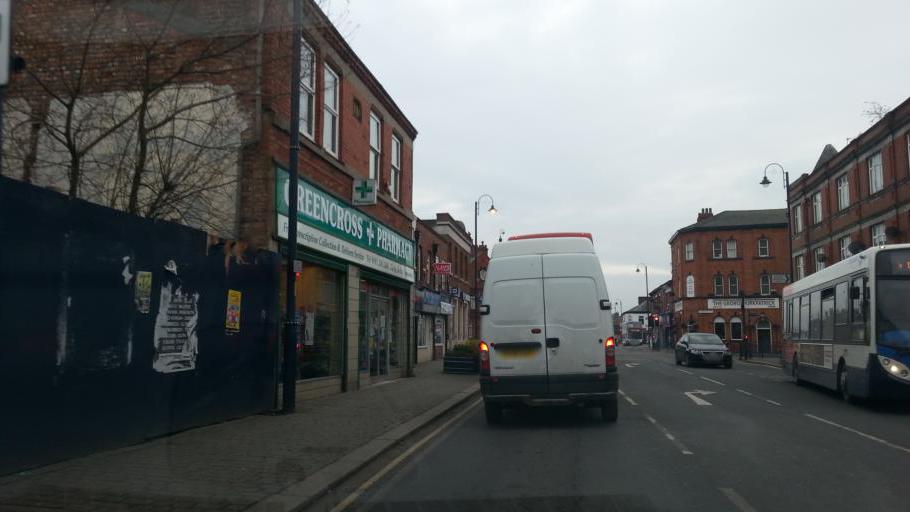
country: GB
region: England
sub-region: Borough of Tameside
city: Denton
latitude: 53.4568
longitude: -2.1141
